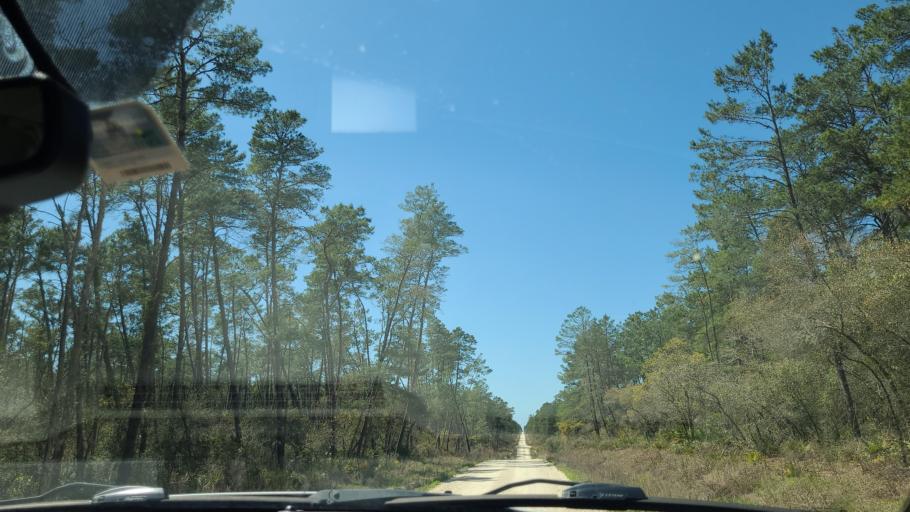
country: US
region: Florida
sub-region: Putnam County
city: Interlachen
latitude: 29.4286
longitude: -81.8304
